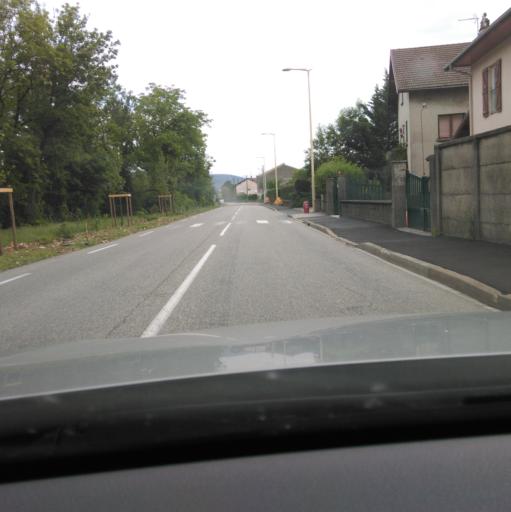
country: FR
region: Rhone-Alpes
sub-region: Departement de l'Ain
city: Izernore
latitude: 46.1895
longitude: 5.5435
